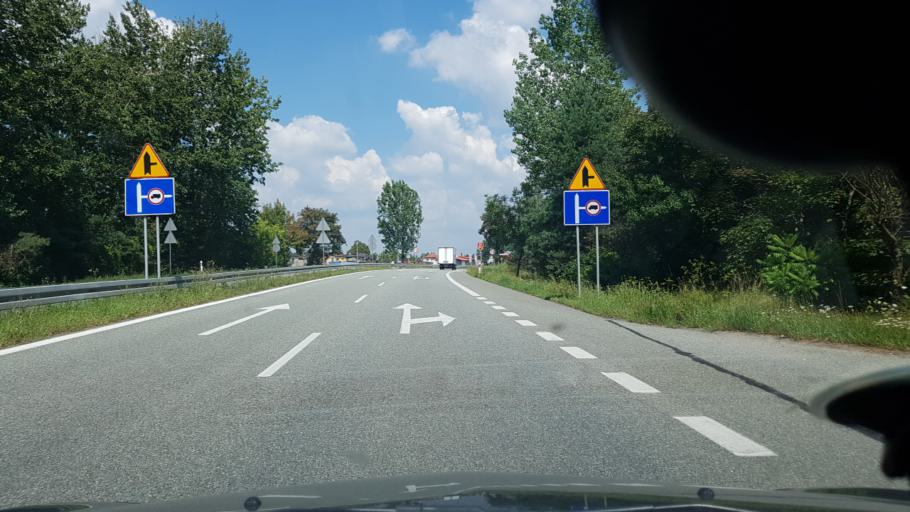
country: PL
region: Silesian Voivodeship
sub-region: Powiat pszczynski
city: Rudziczka
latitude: 50.0839
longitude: 18.7539
